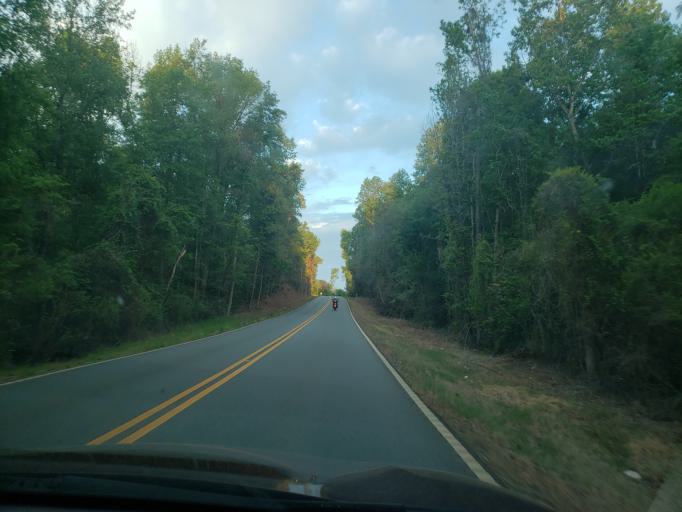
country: US
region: Alabama
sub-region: Tallapoosa County
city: Dadeville
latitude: 32.7105
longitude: -85.7794
